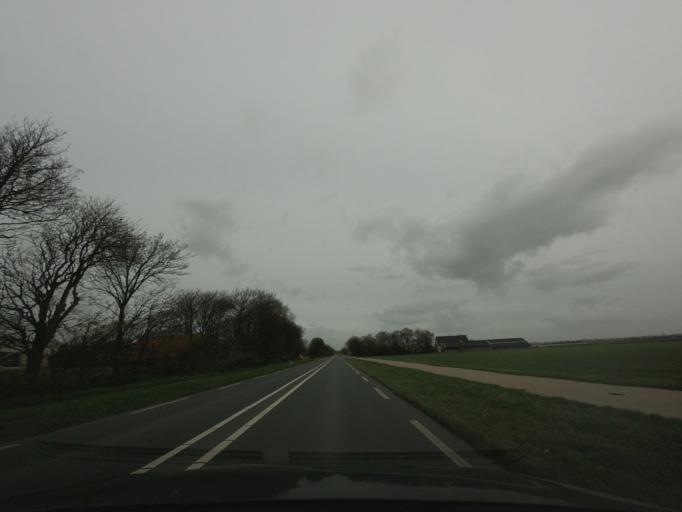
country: NL
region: North Holland
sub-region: Gemeente Opmeer
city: Opmeer
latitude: 52.7931
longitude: 4.9842
